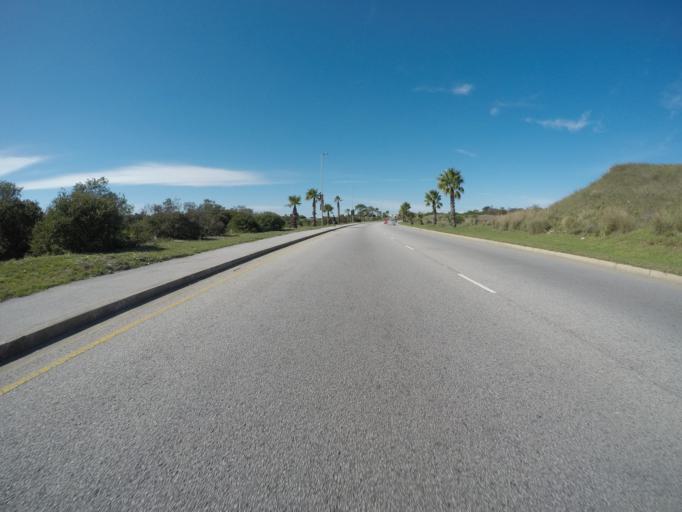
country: ZA
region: Eastern Cape
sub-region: Nelson Mandela Bay Metropolitan Municipality
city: Port Elizabeth
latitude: -33.9867
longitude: 25.6435
